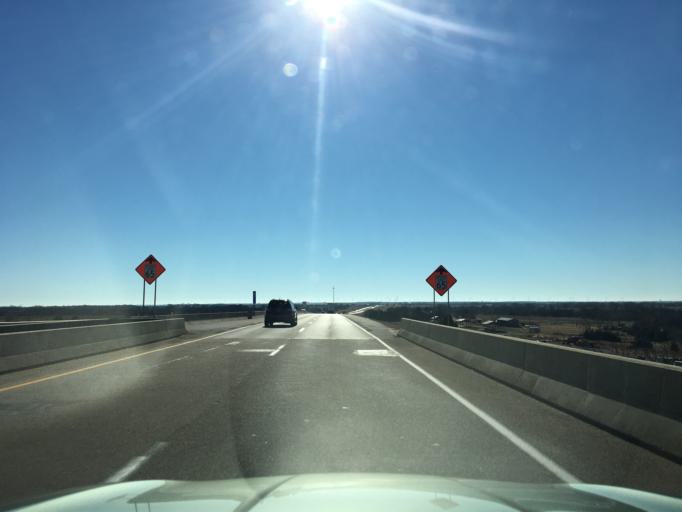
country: US
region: Kansas
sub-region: Sumner County
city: Wellington
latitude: 37.2656
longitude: -97.3400
